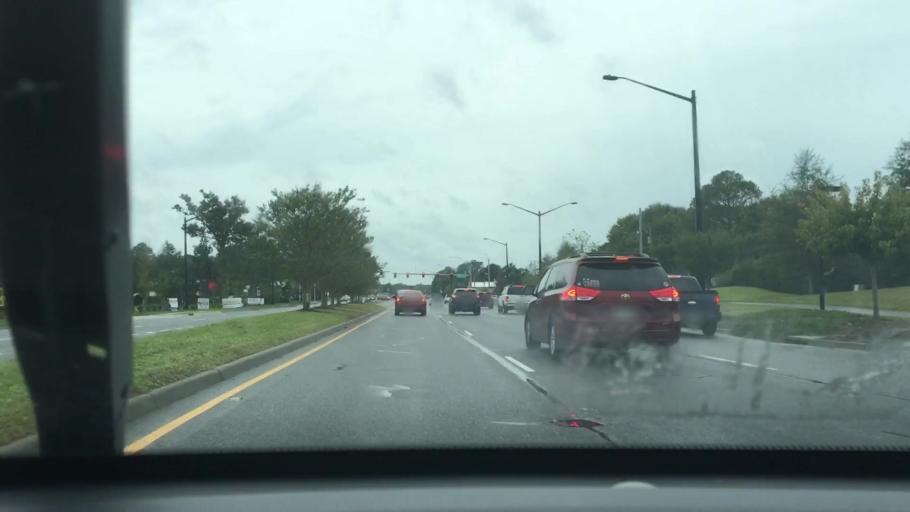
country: US
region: Virginia
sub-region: City of Virginia Beach
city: Virginia Beach
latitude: 36.8075
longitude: -76.0774
